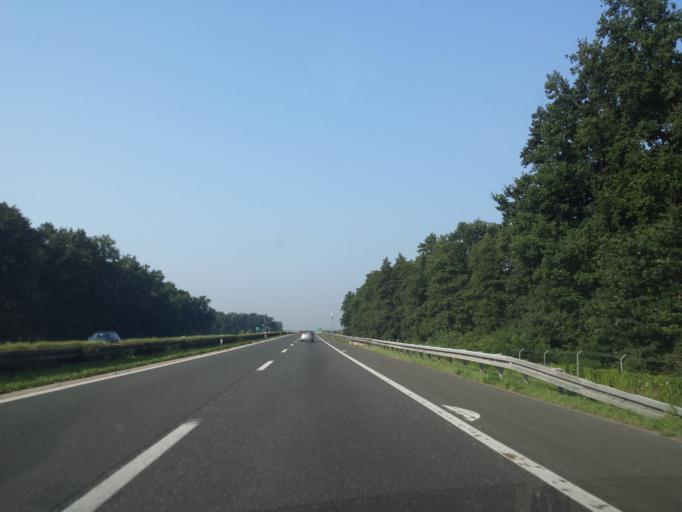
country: HR
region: Karlovacka
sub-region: Grad Karlovac
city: Karlovac
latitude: 45.5276
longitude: 15.5683
